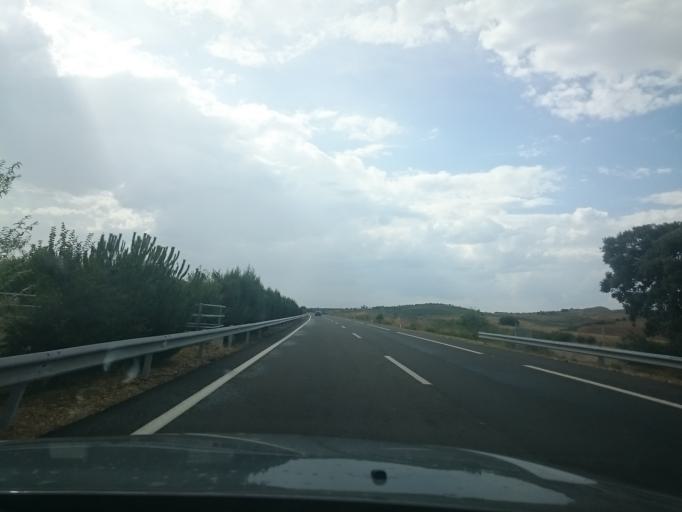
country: ES
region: Navarre
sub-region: Provincia de Navarra
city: Sartaguda
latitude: 42.3733
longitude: -2.0843
